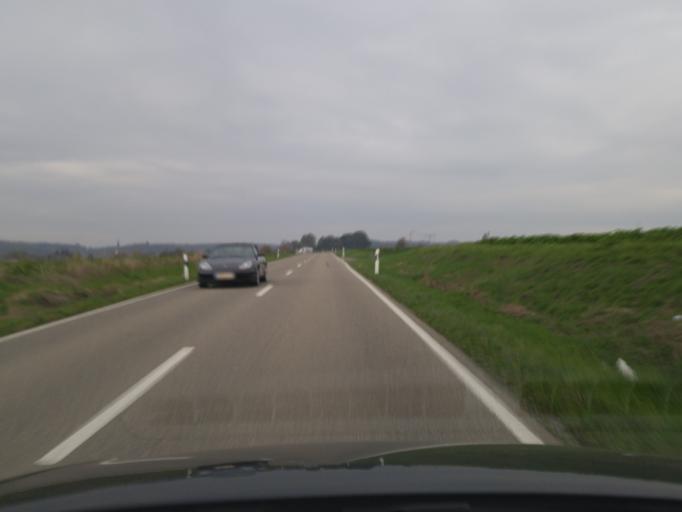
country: DE
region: Baden-Wuerttemberg
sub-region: Regierungsbezirk Stuttgart
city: Bretzfeld
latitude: 49.1692
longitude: 9.4175
